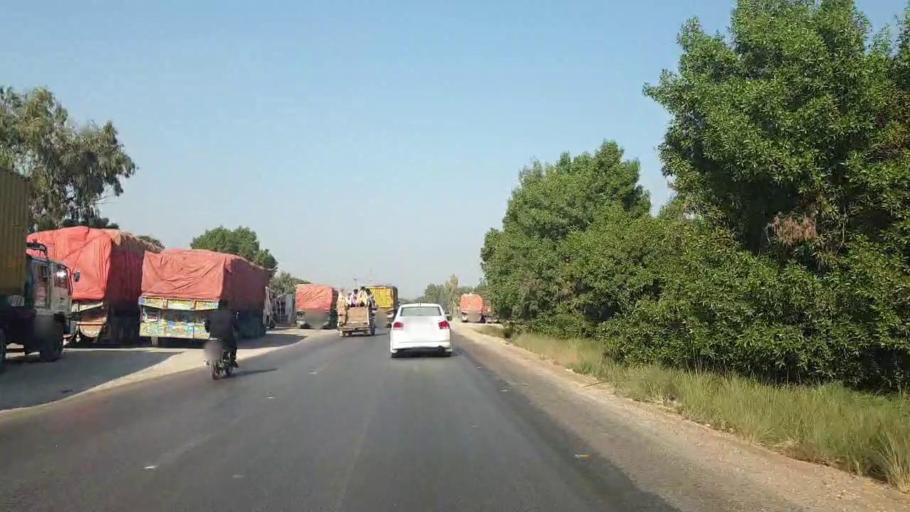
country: PK
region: Sindh
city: Matiari
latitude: 25.5114
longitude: 68.4282
